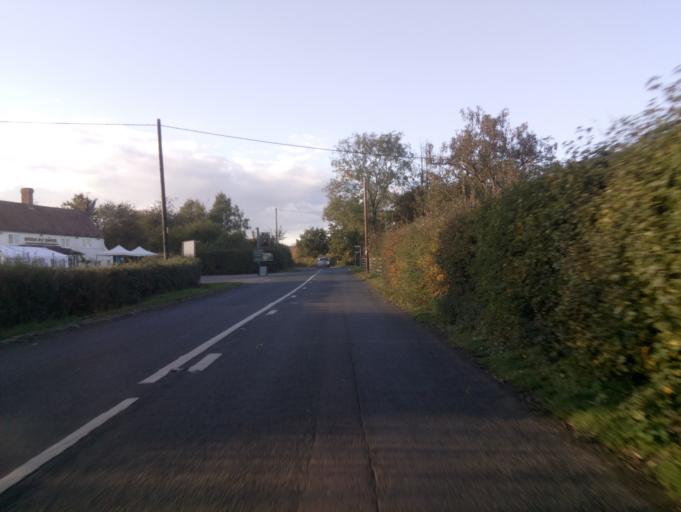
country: GB
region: England
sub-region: Worcestershire
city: Great Malvern
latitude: 52.0172
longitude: -2.3187
